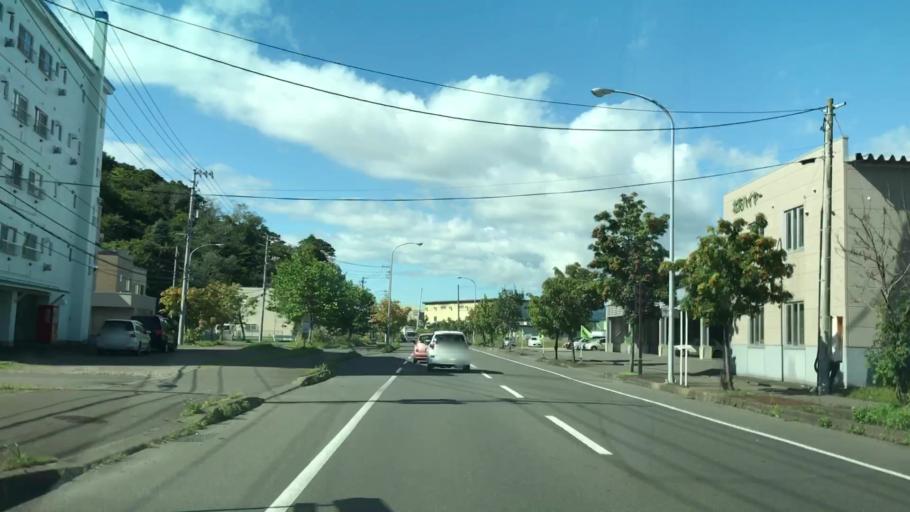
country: JP
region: Hokkaido
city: Muroran
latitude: 42.3277
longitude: 140.9679
